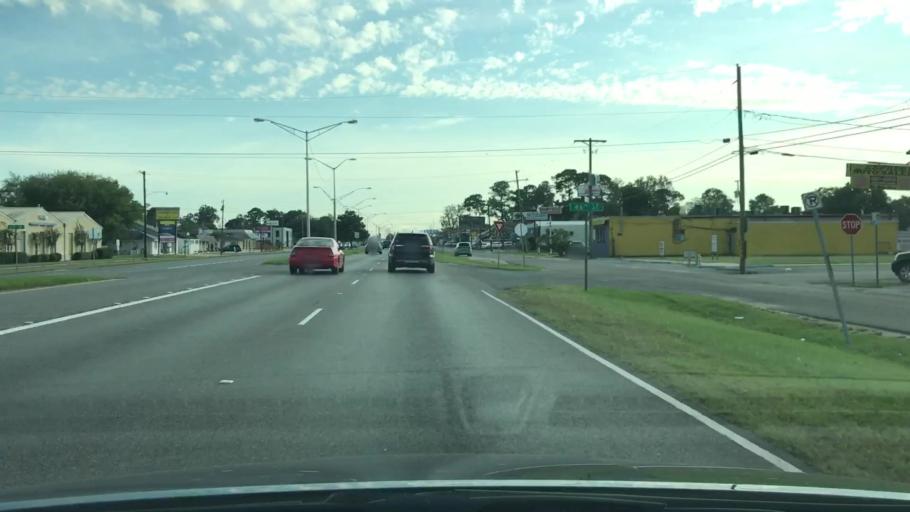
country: US
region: Louisiana
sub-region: Jefferson Parish
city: Metairie
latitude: 29.9856
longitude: -90.1561
